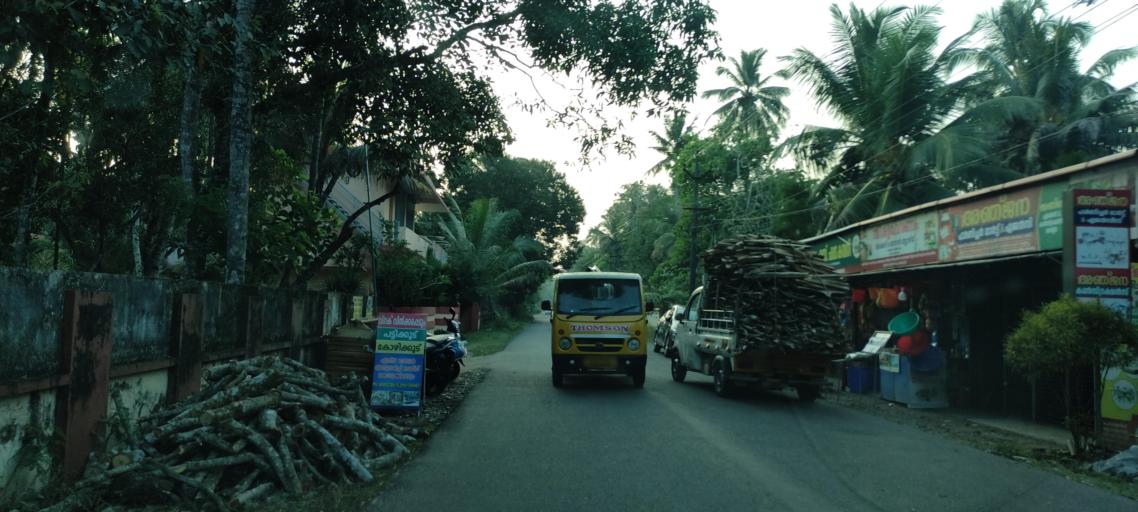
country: IN
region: Kerala
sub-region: Alappuzha
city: Kayankulam
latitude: 9.1353
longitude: 76.5334
